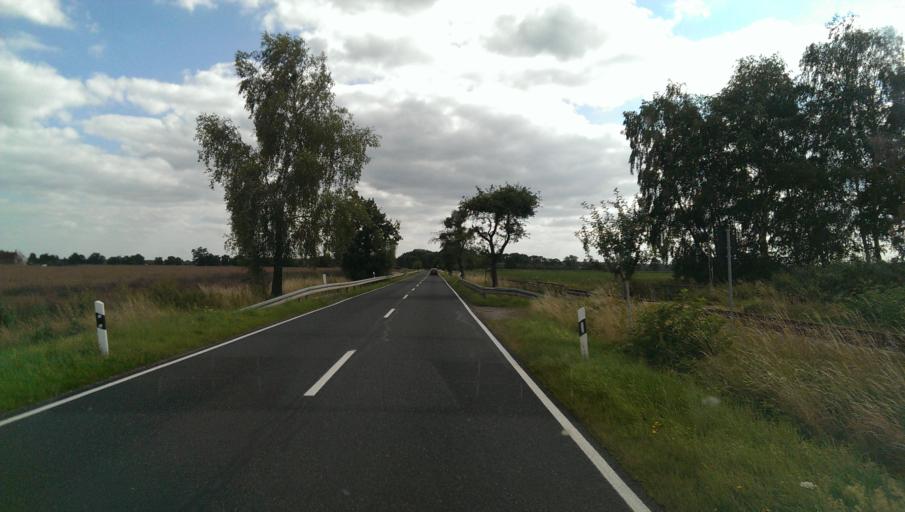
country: DE
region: Saxony-Anhalt
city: Worlitz
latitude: 51.8225
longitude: 12.4095
